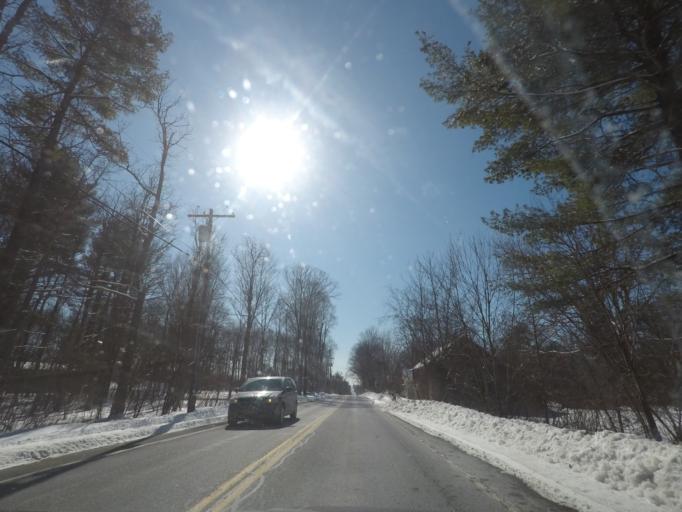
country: US
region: New York
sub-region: Saratoga County
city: Ballston Spa
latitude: 42.9768
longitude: -73.8318
